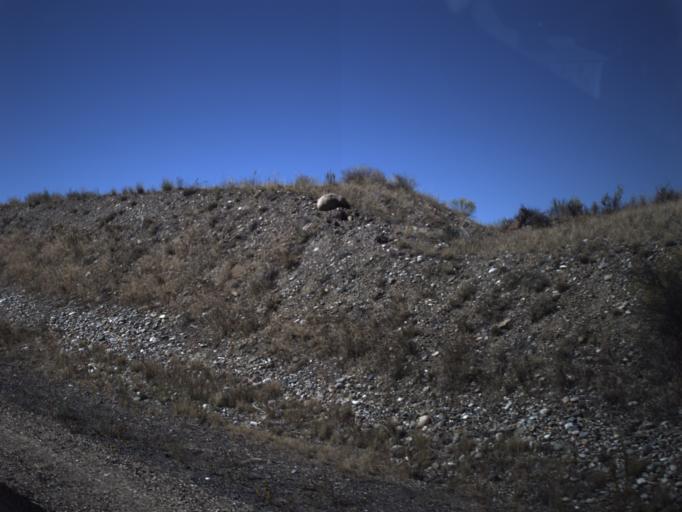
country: US
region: Utah
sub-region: Garfield County
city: Panguitch
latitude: 37.6218
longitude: -111.8661
